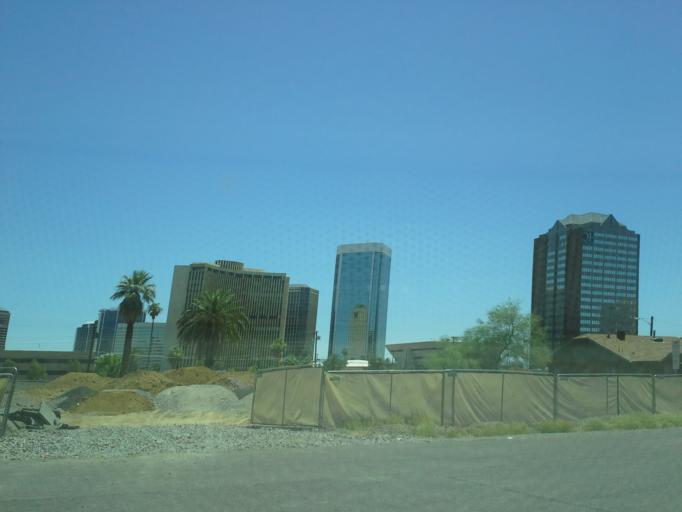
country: US
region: Arizona
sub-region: Maricopa County
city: Phoenix
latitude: 33.4912
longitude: -112.0716
